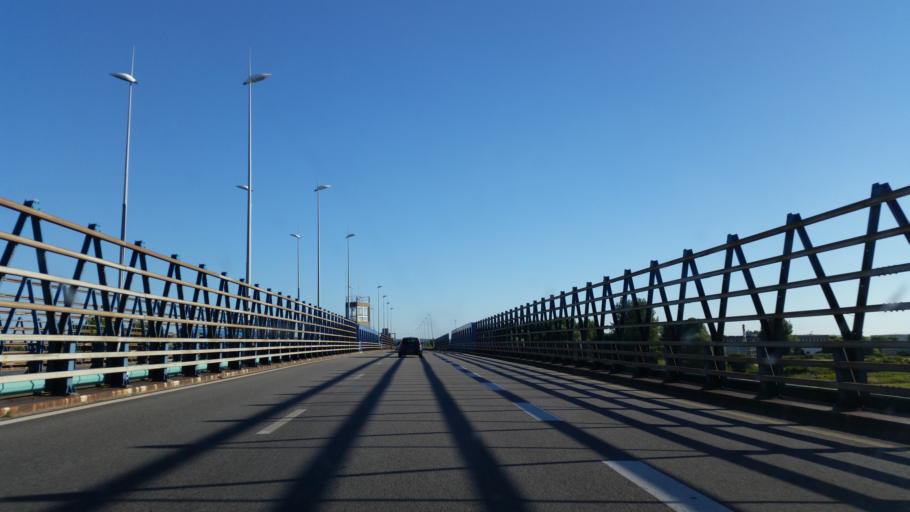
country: FR
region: Haute-Normandie
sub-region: Departement de la Seine-Maritime
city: Rogerville
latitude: 49.4909
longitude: 0.2650
